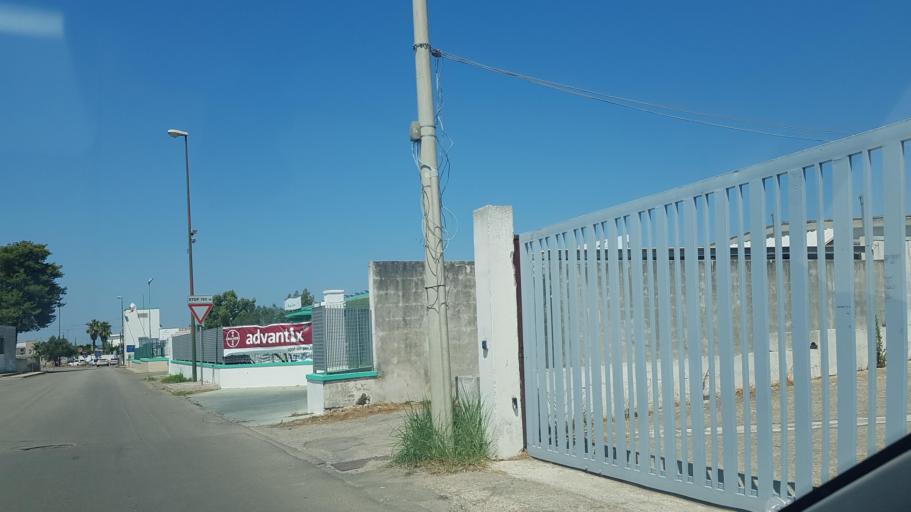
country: IT
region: Apulia
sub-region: Provincia di Lecce
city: Melendugno
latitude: 40.2775
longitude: 18.3442
